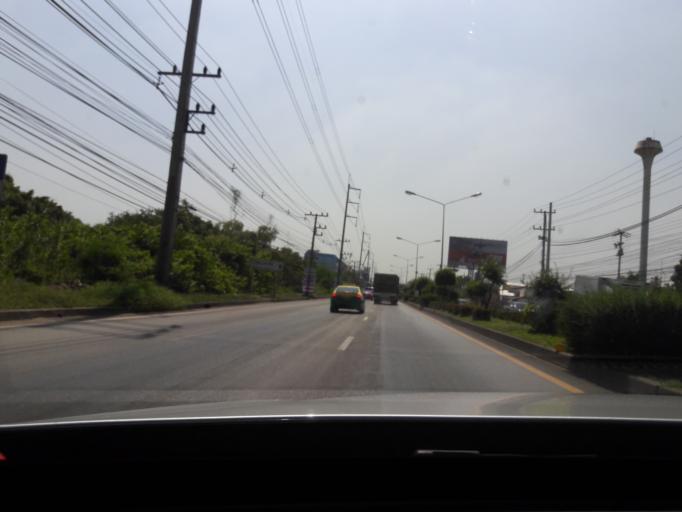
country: TH
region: Samut Sakhon
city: Samut Sakhon
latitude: 13.5918
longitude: 100.2811
